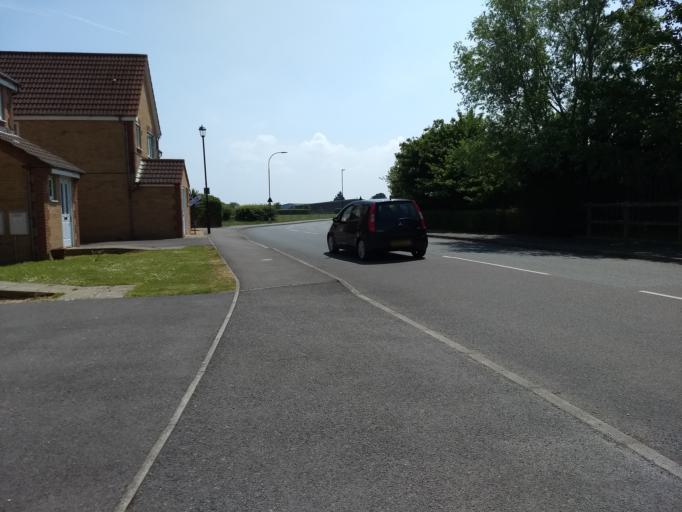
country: GB
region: England
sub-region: Isle of Wight
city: Northwood
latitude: 50.7529
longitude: -1.3079
